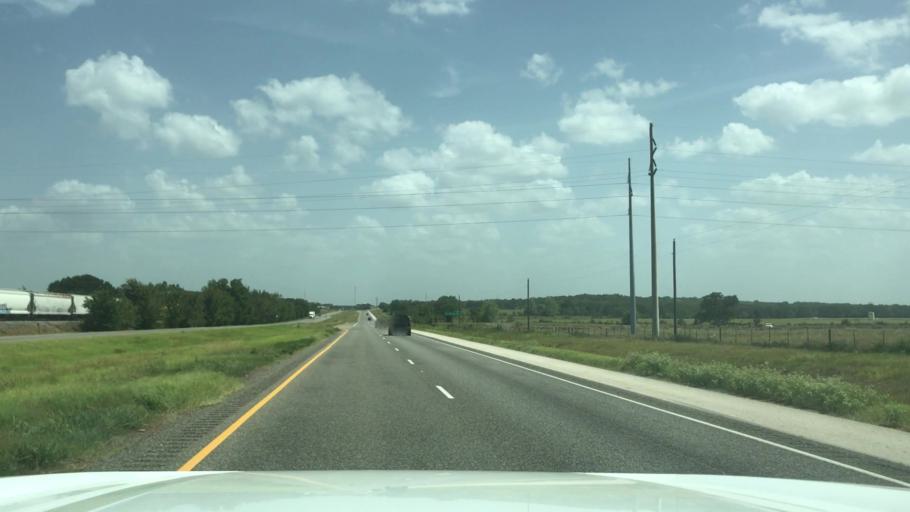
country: US
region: Texas
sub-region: Robertson County
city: Hearne
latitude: 30.9186
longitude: -96.6209
